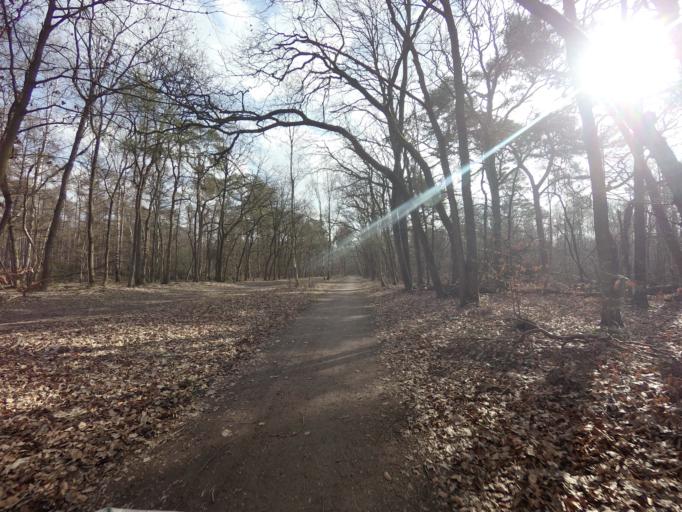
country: NL
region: North Holland
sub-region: Gemeente Bussum
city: Bussum
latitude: 52.2502
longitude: 5.1464
